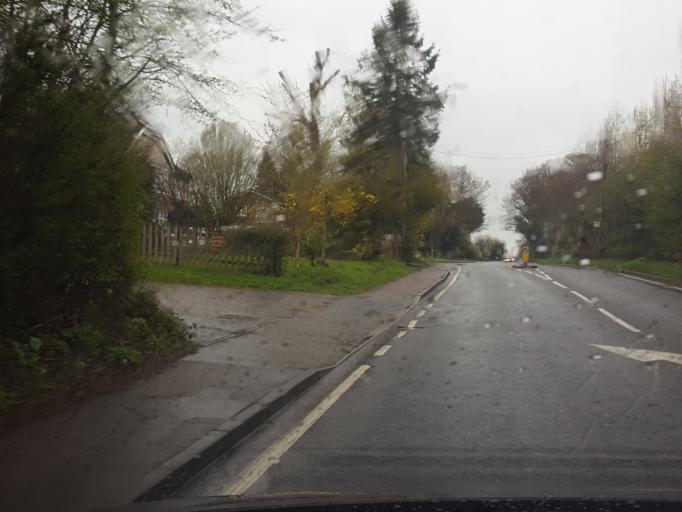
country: GB
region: England
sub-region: Essex
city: Great Horkesley
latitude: 51.9239
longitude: 0.8831
